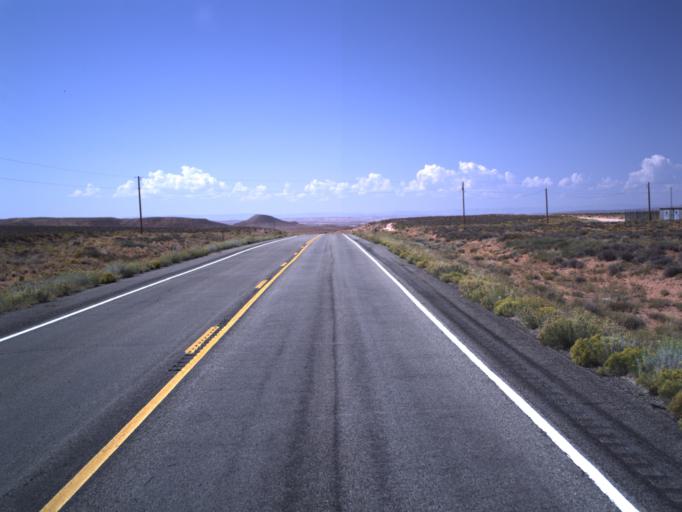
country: US
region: Utah
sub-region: San Juan County
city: Blanding
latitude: 37.0189
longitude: -109.6082
